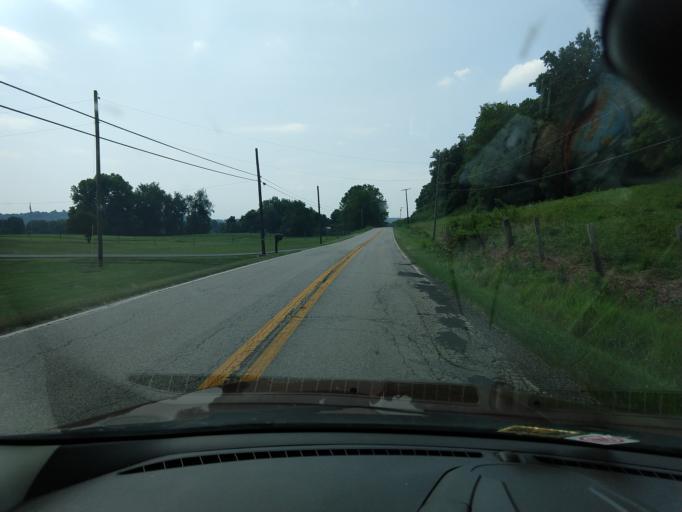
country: US
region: West Virginia
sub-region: Mason County
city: New Haven
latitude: 38.9299
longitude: -81.9143
